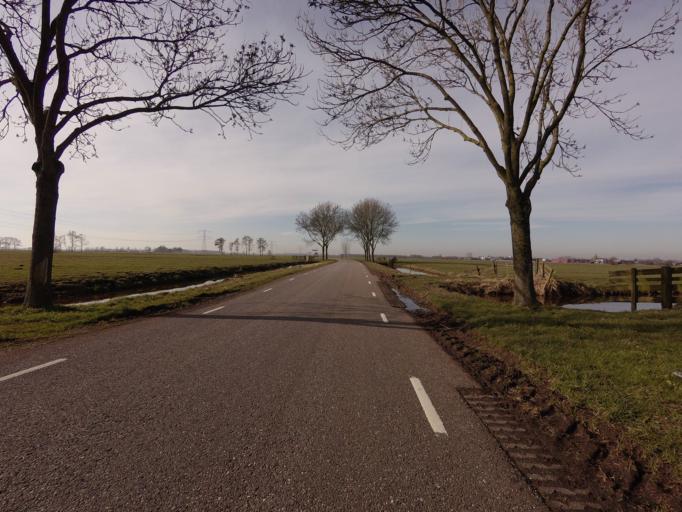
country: NL
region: South Holland
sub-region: Gemeente Sliedrecht
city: Sliedrecht
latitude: 51.8614
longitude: 4.7918
